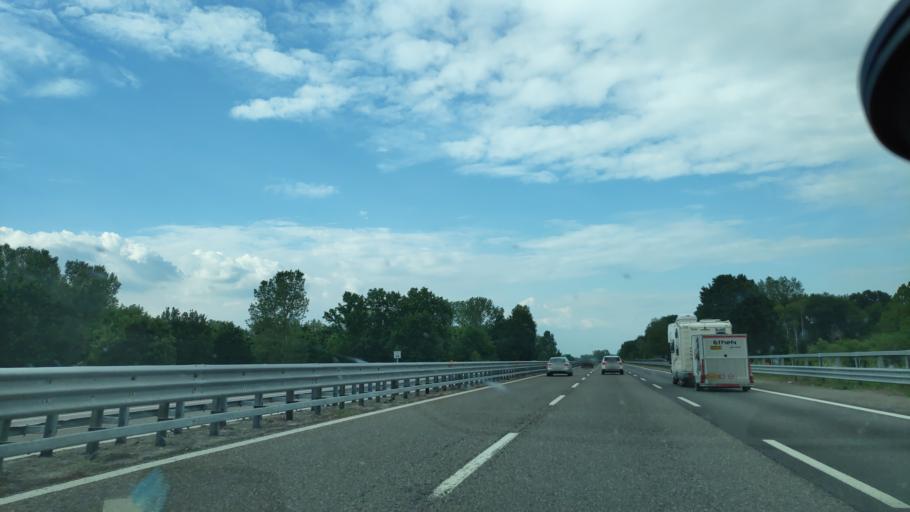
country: IT
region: Lombardy
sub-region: Provincia di Pavia
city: Gropello Cairoli
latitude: 45.1863
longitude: 9.0113
